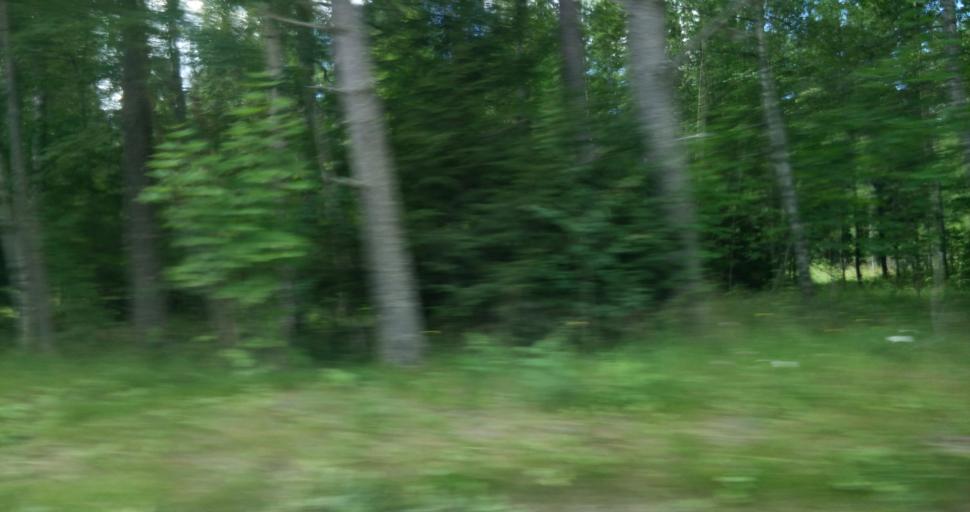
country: SE
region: Vaermland
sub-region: Hagfors Kommun
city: Ekshaerad
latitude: 60.0518
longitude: 13.4829
